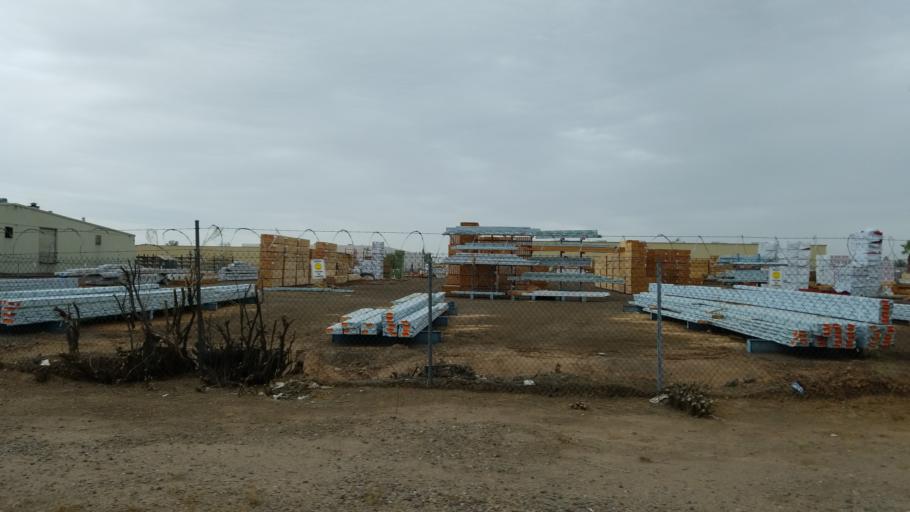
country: US
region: Arizona
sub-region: Maricopa County
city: Phoenix
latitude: 33.4467
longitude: -112.1536
